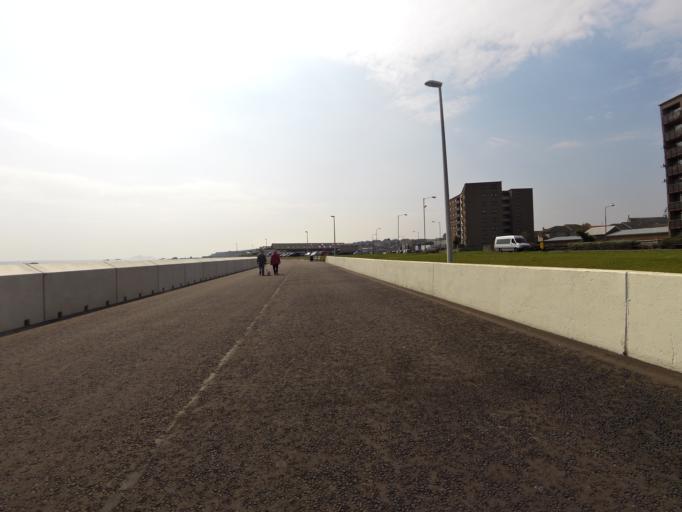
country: GB
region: Scotland
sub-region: Fife
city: Kirkcaldy
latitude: 56.1013
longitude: -3.1599
